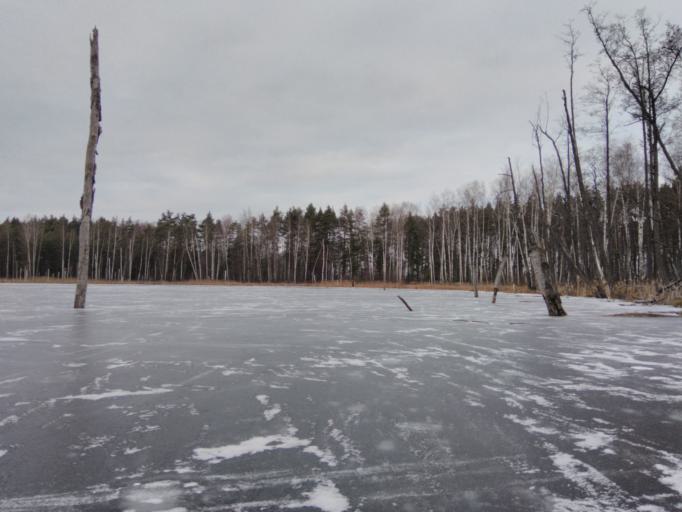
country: RU
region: Vladimir
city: Sobinka
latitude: 55.9673
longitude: 40.0543
